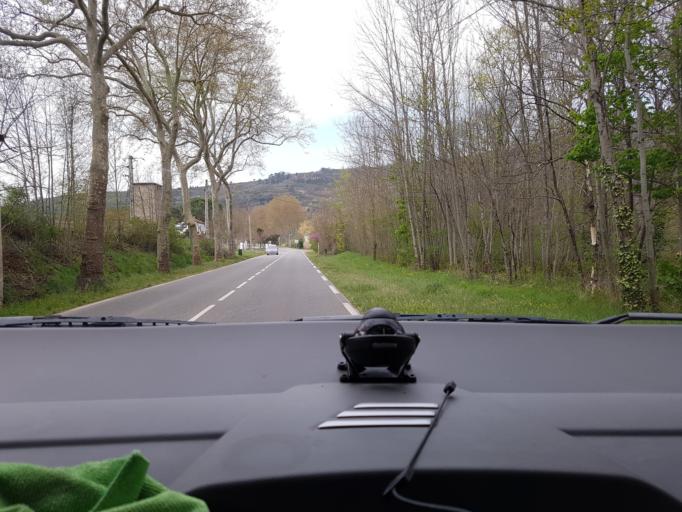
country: FR
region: Languedoc-Roussillon
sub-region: Departement de l'Aude
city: Couiza
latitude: 42.9558
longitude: 2.2589
